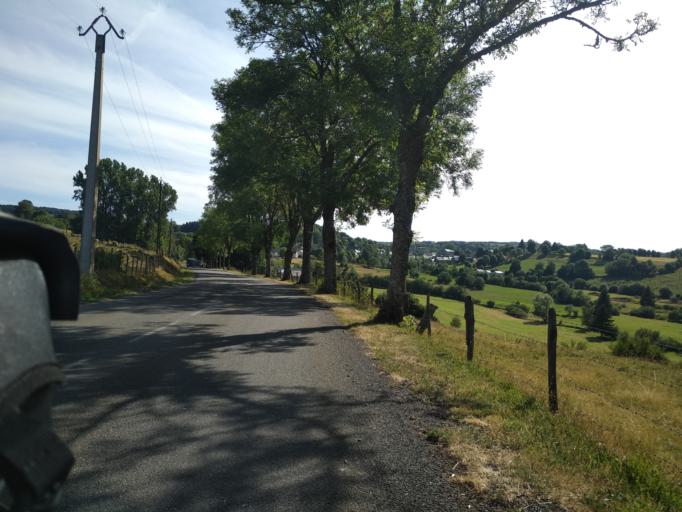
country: FR
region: Auvergne
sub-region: Departement du Cantal
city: Chaudes-Aigues
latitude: 44.6678
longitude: 3.0554
